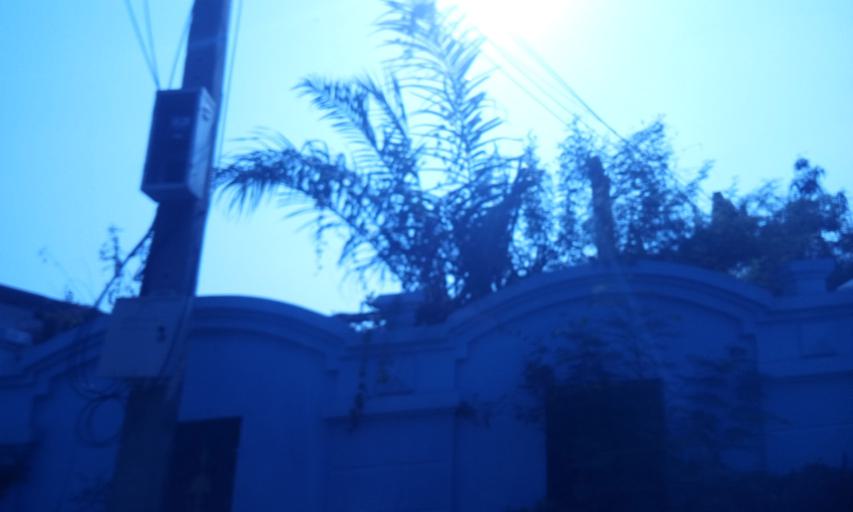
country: TH
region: Pathum Thani
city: Lam Luk Ka
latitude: 13.9572
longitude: 100.7058
